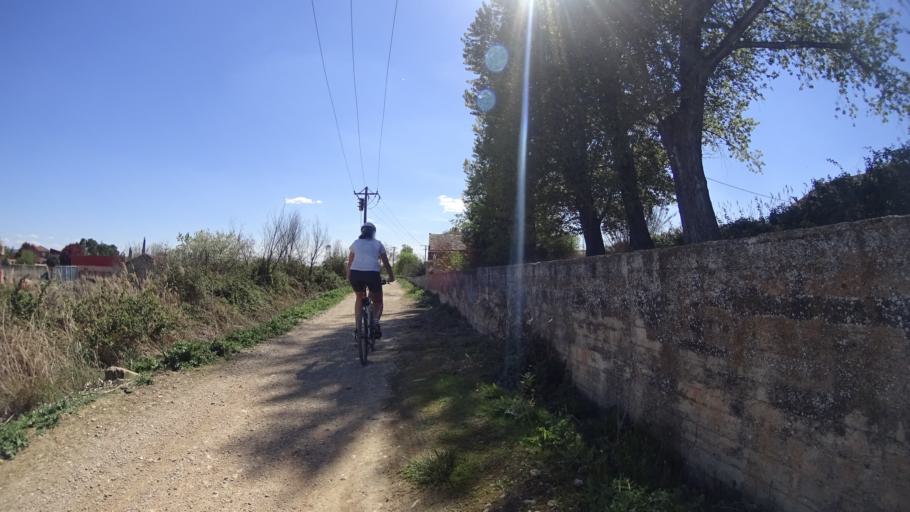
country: ES
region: Castille and Leon
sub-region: Provincia de Valladolid
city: Santovenia de Pisuerga
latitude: 41.6968
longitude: -4.7132
